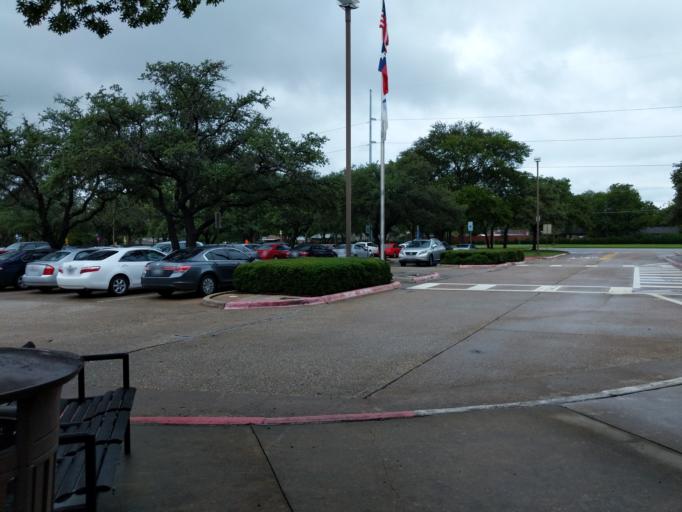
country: US
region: Texas
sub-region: Dallas County
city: Richardson
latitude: 32.9598
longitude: -96.7325
